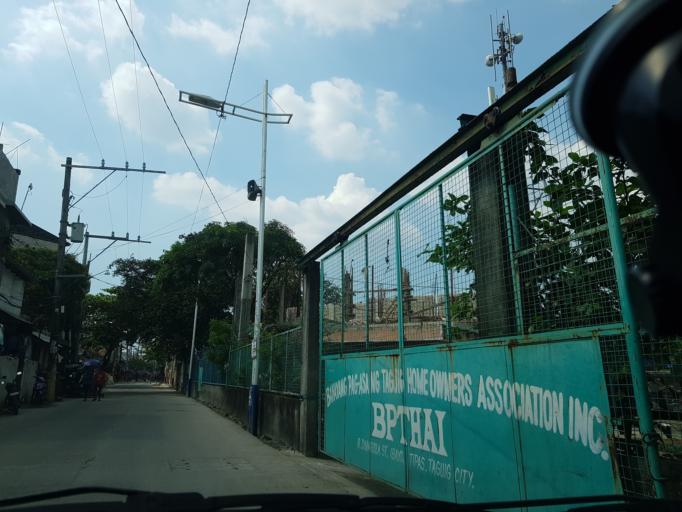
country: PH
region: Calabarzon
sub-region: Province of Rizal
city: Pateros
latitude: 14.5457
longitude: 121.0837
